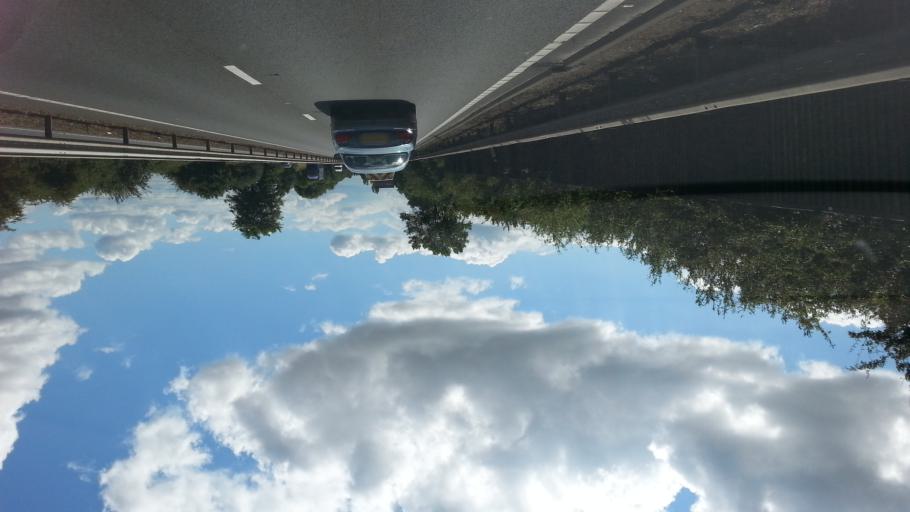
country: GB
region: England
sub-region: Cambridgeshire
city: Eaton Socon
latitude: 52.2261
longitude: -0.2948
